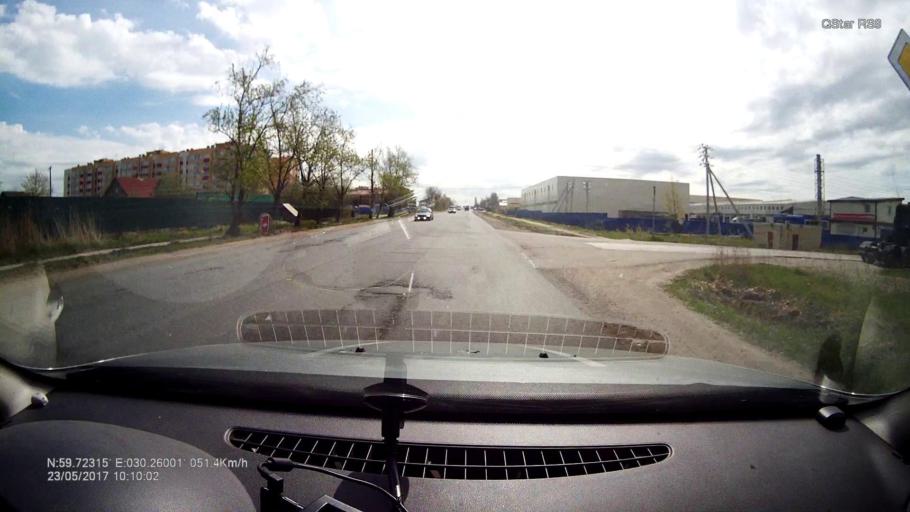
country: RU
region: St.-Petersburg
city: Aleksandrovskaya
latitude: 59.7231
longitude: 30.2601
